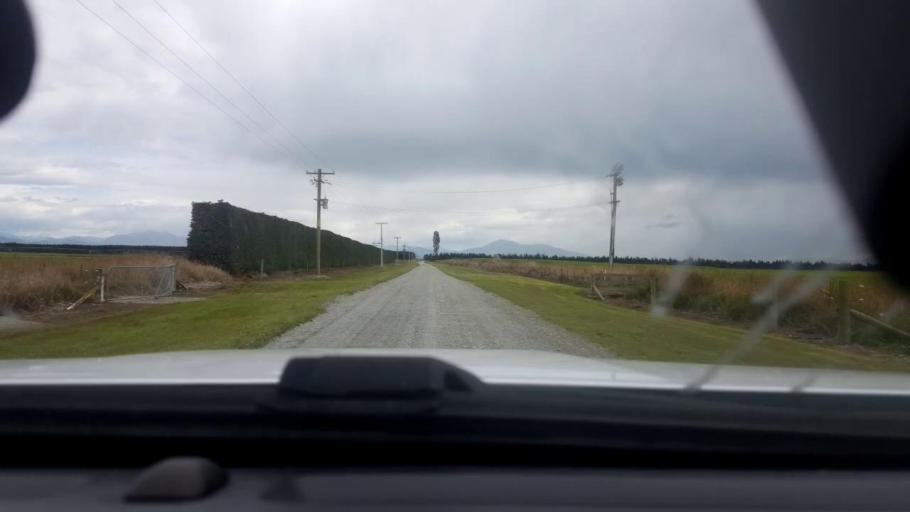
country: NZ
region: Canterbury
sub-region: Timaru District
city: Timaru
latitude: -44.1725
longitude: 171.4166
